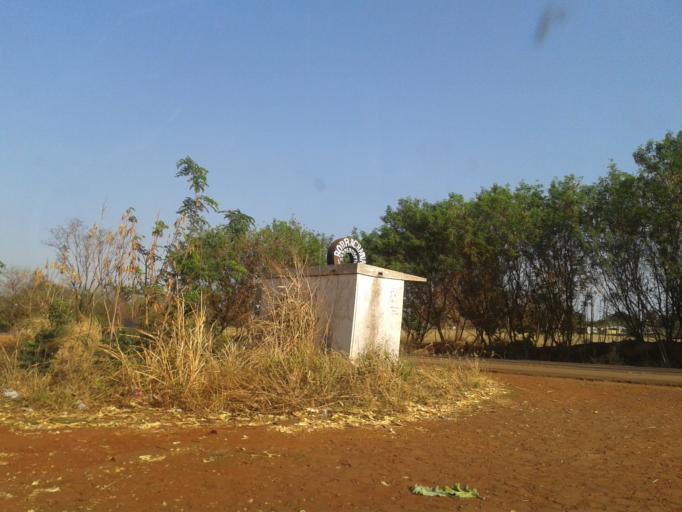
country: BR
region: Minas Gerais
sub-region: Ituiutaba
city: Ituiutaba
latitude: -18.9650
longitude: -49.4813
